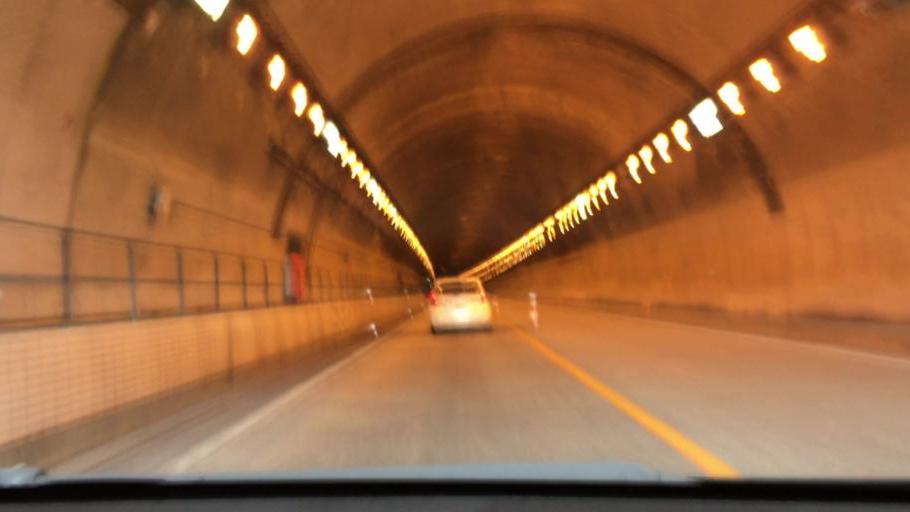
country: JP
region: Yamaguchi
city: Tokuyama
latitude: 34.0891
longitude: 131.7756
